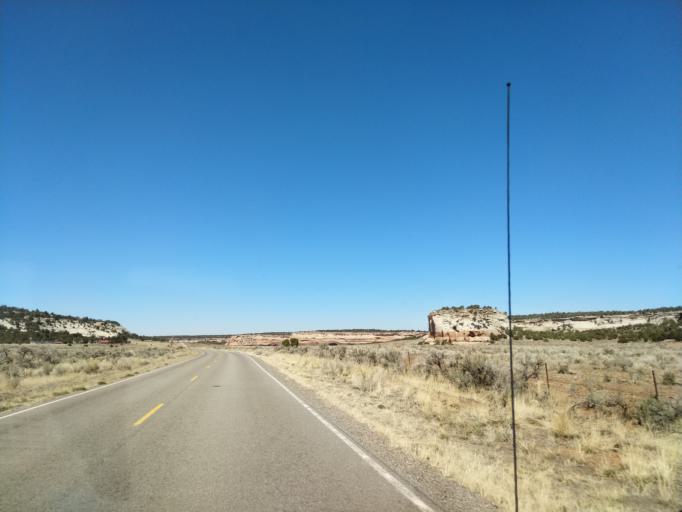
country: US
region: Colorado
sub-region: Mesa County
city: Fruita
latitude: 38.9956
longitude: -108.8257
